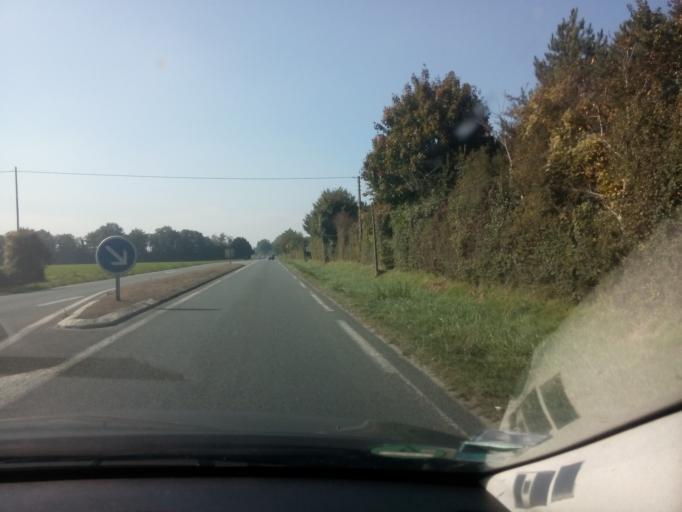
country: FR
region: Pays de la Loire
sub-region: Departement de Maine-et-Loire
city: Pellouailles-les-Vignes
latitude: 47.5335
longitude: -0.4146
